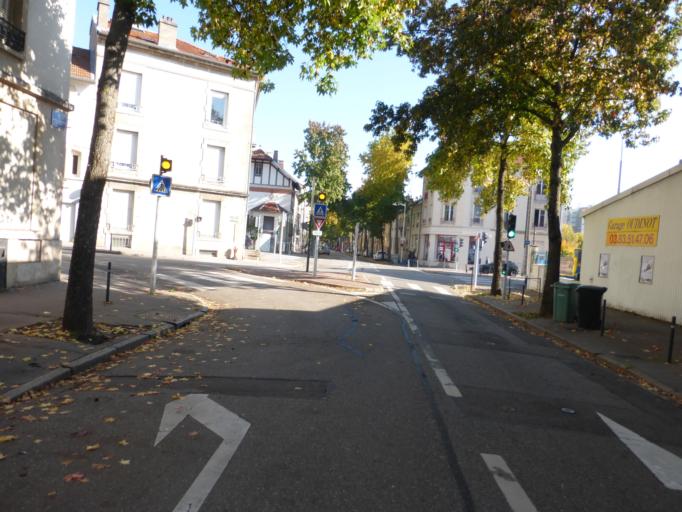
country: FR
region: Lorraine
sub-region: Departement de Meurthe-et-Moselle
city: Nancy
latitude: 48.6726
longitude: 6.1763
